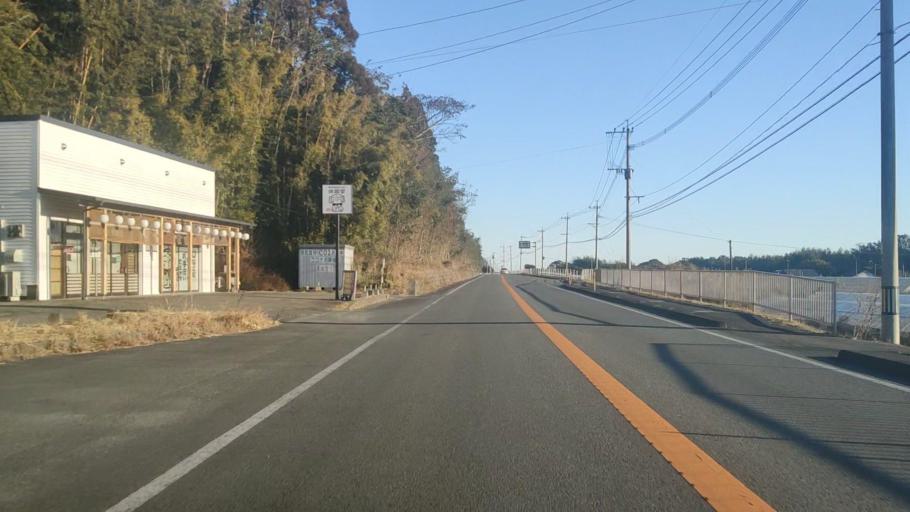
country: JP
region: Miyazaki
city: Takanabe
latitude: 32.1004
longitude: 131.5201
